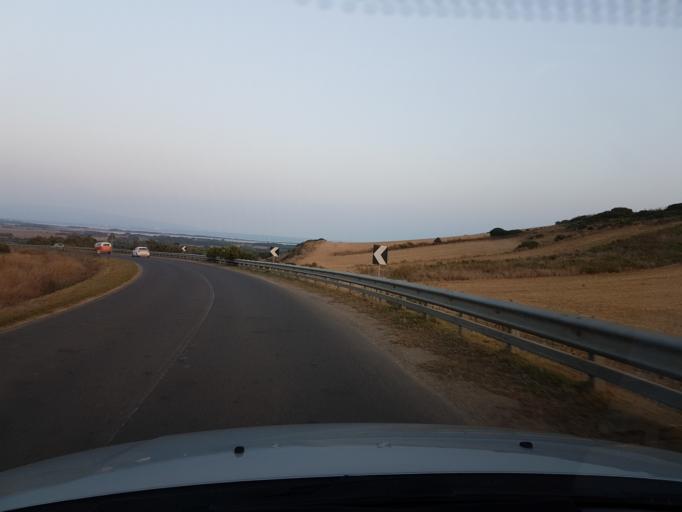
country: IT
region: Sardinia
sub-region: Provincia di Oristano
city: Cabras
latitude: 39.9320
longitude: 8.4490
